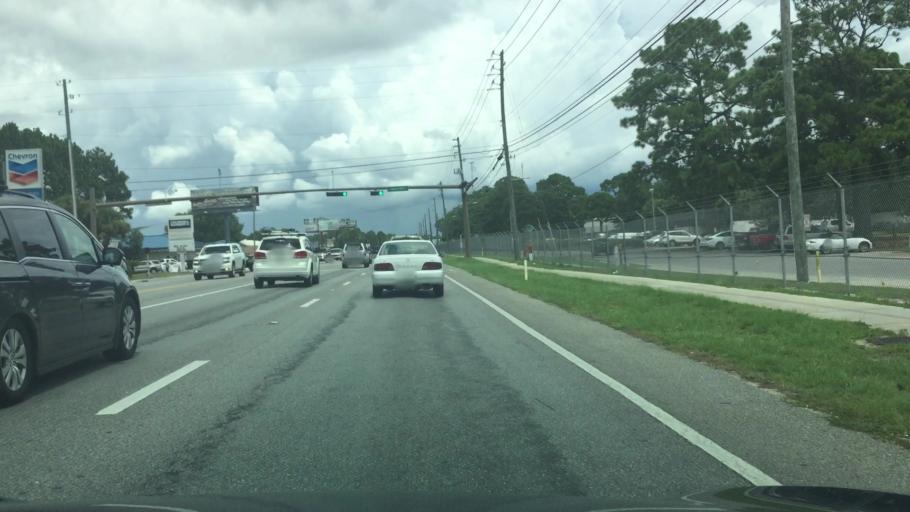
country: US
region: Florida
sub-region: Bay County
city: Upper Grand Lagoon
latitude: 30.1780
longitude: -85.7603
